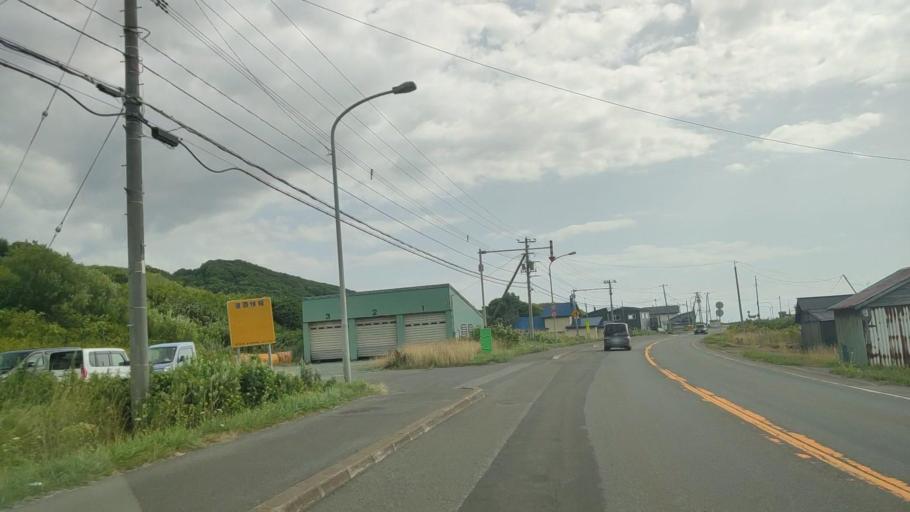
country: JP
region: Hokkaido
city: Rumoi
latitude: 44.1437
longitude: 141.6549
